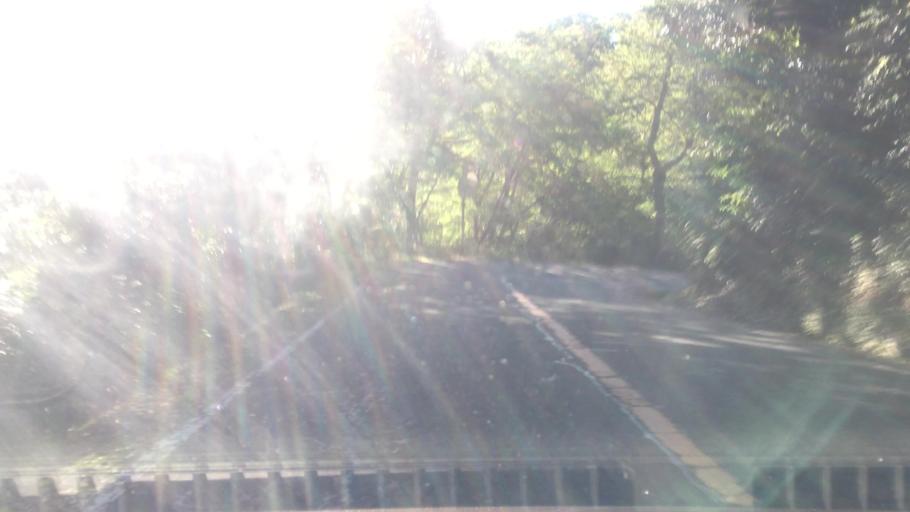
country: JP
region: Hyogo
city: Toyooka
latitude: 35.6204
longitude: 134.8720
